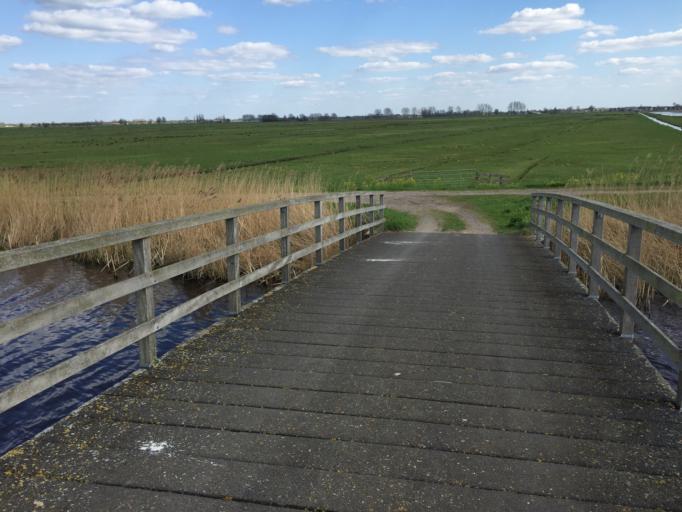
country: NL
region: South Holland
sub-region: Gemeente Sliedrecht
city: Sliedrecht
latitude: 51.8900
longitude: 4.7725
